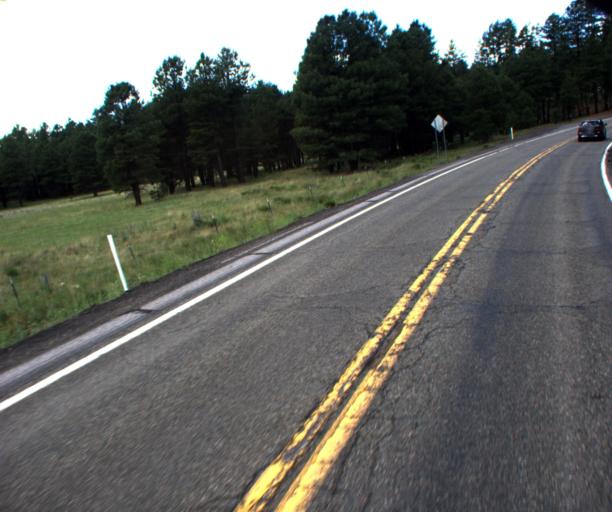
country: US
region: Arizona
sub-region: Coconino County
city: Flagstaff
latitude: 35.2679
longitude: -111.7388
